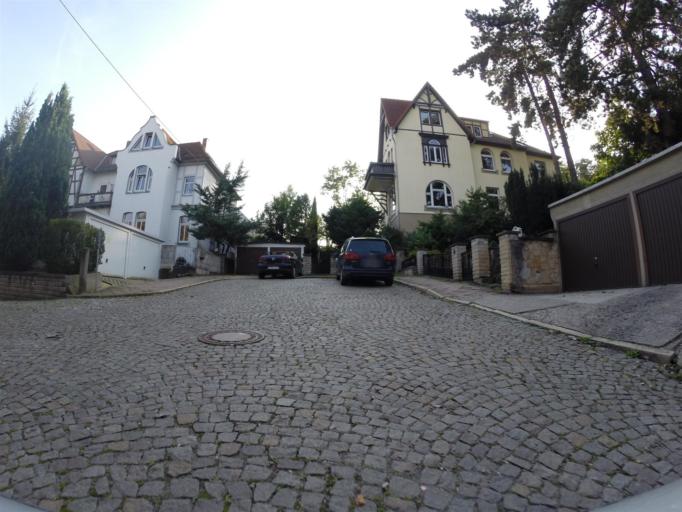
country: DE
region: Thuringia
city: Jena
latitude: 50.9304
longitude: 11.5687
